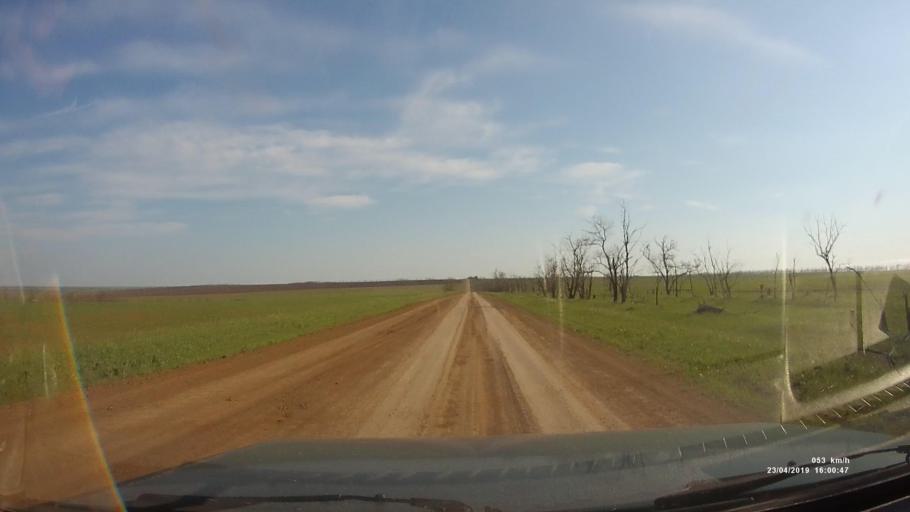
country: RU
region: Rostov
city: Remontnoye
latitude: 46.5067
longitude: 43.1070
